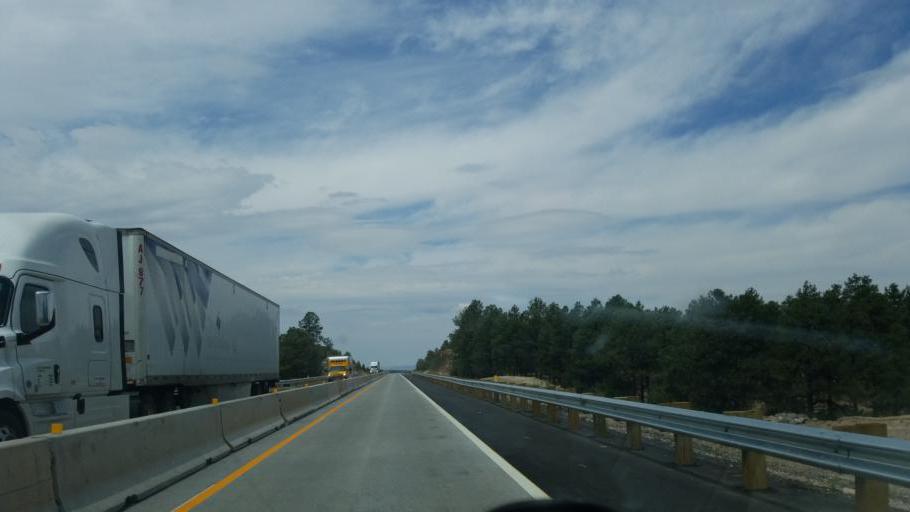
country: US
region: Arizona
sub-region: Coconino County
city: Williams
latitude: 35.2225
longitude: -112.2487
